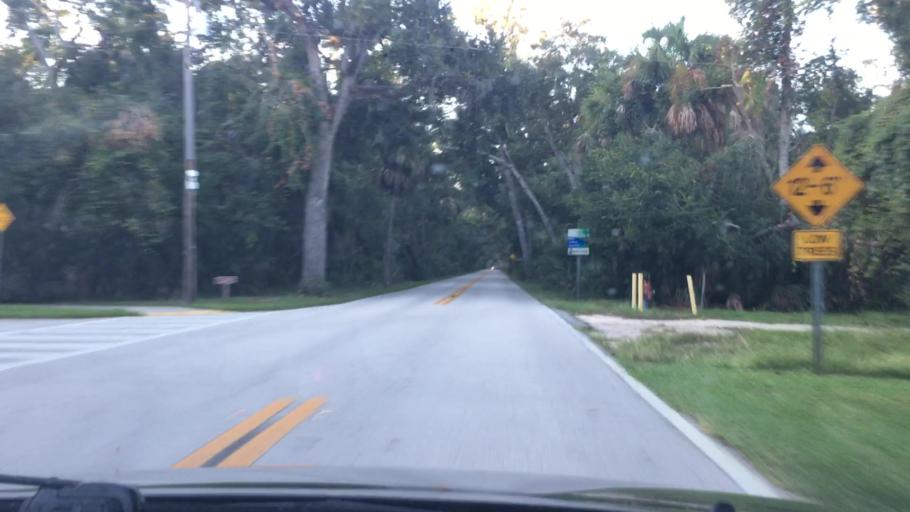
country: US
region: Florida
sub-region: Volusia County
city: Ormond-by-the-Sea
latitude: 29.3276
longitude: -81.0770
